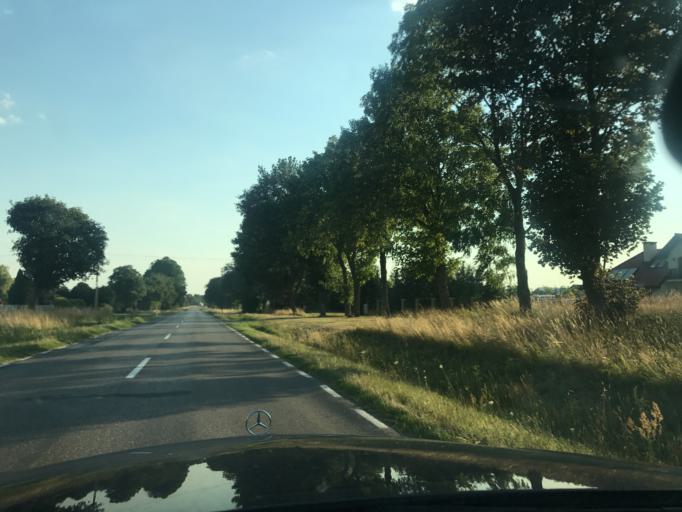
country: PL
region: Lublin Voivodeship
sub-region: Powiat bialski
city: Wisznice
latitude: 51.7571
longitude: 23.1764
